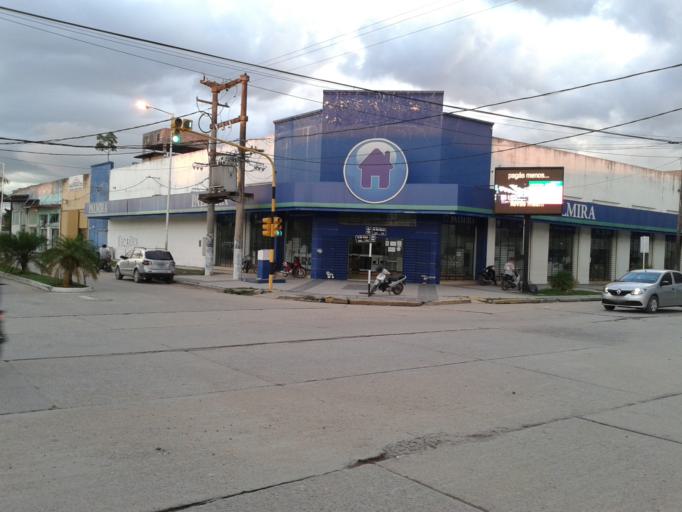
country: AR
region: Formosa
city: Clorinda
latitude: -25.2871
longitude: -57.7117
